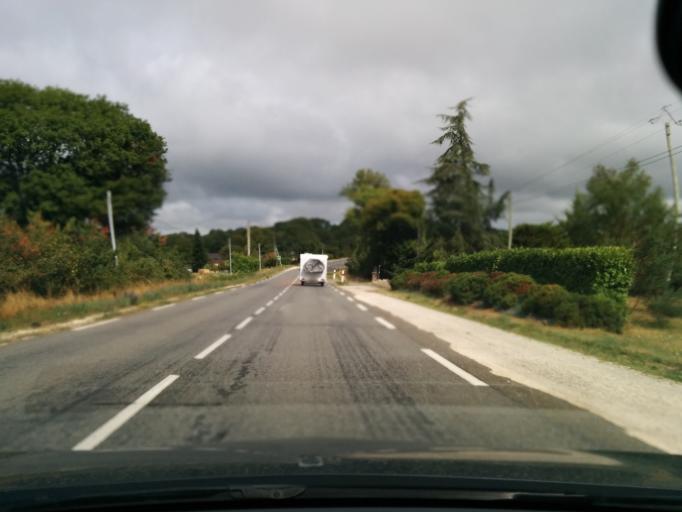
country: FR
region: Midi-Pyrenees
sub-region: Departement du Lot
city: Le Vigan
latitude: 44.6285
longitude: 1.4892
